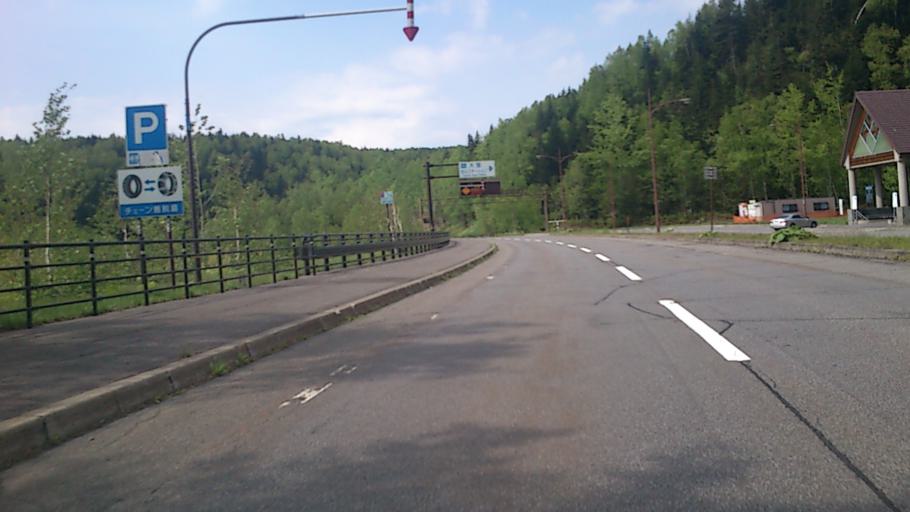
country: JP
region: Hokkaido
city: Kamikawa
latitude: 43.6657
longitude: 143.0367
